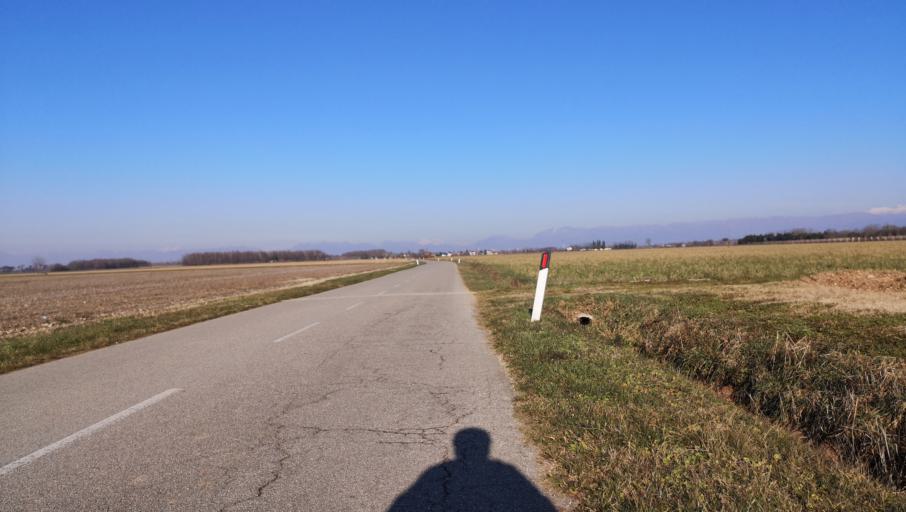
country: IT
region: Friuli Venezia Giulia
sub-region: Provincia di Udine
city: Santa Maria la Longa
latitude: 45.9401
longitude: 13.2785
